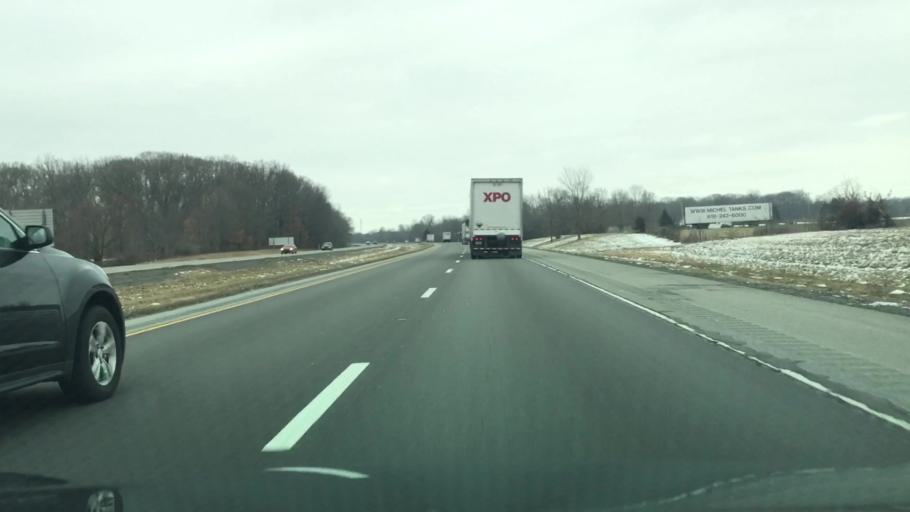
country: US
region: Illinois
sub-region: Jefferson County
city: Ina
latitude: 38.1744
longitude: -88.9058
